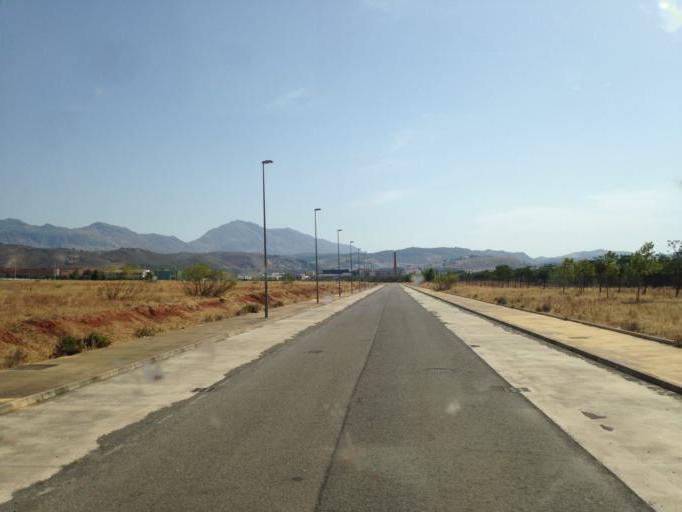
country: ES
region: Andalusia
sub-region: Provincia de Malaga
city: Antequera
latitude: 37.0392
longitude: -4.5236
